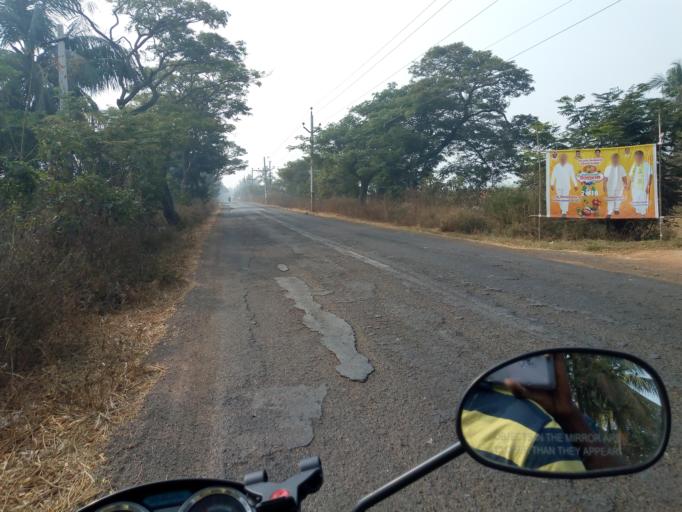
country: IN
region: Andhra Pradesh
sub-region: West Godavari
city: Tadepallegudem
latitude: 16.7598
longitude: 81.4240
